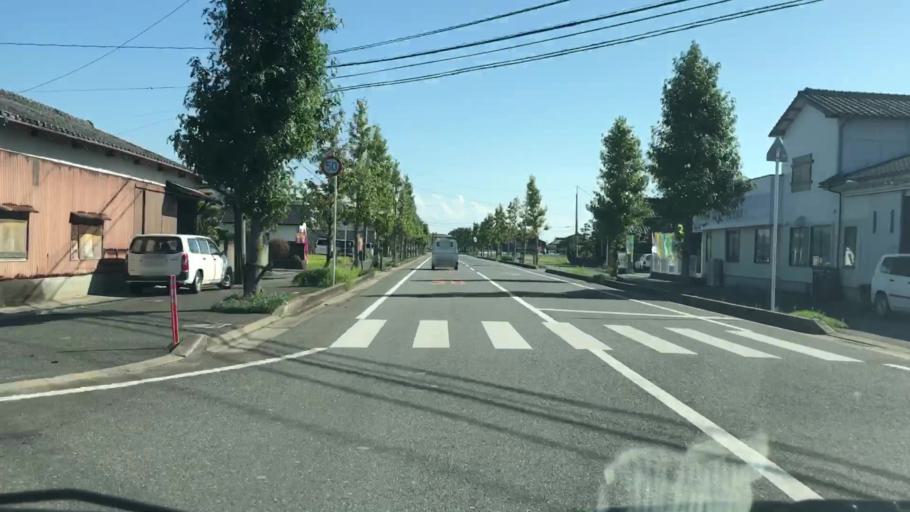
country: JP
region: Saga Prefecture
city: Okawa
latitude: 33.1886
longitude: 130.3143
